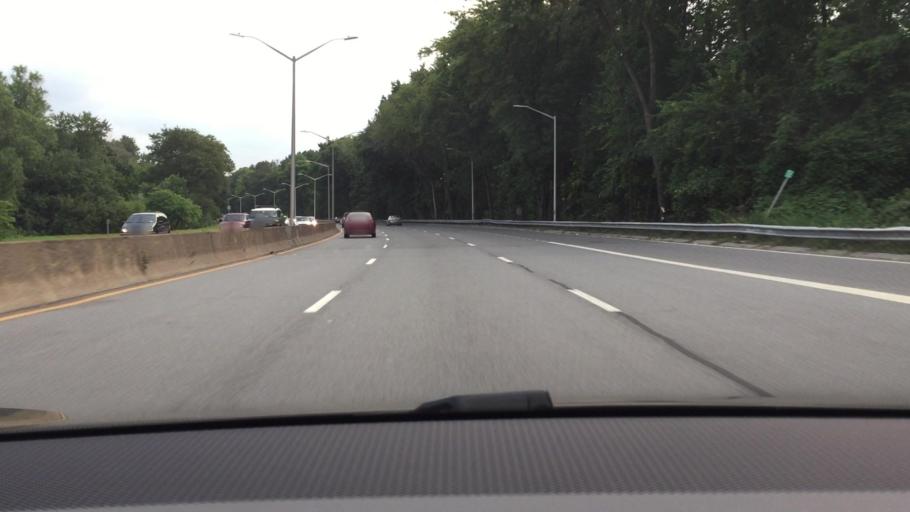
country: US
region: New York
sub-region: Bronx
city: Eastchester
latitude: 40.8934
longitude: -73.8634
